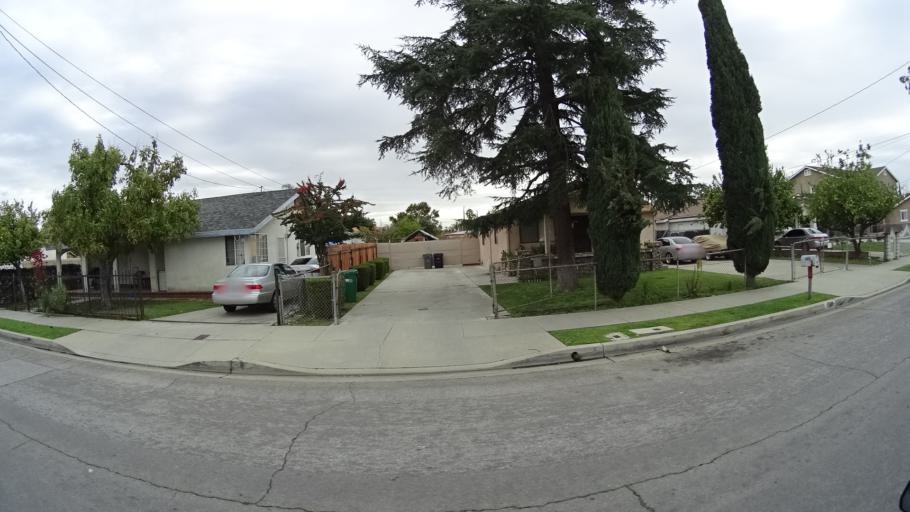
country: US
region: California
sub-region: Los Angeles County
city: Irwindale
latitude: 34.1026
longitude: -117.9463
